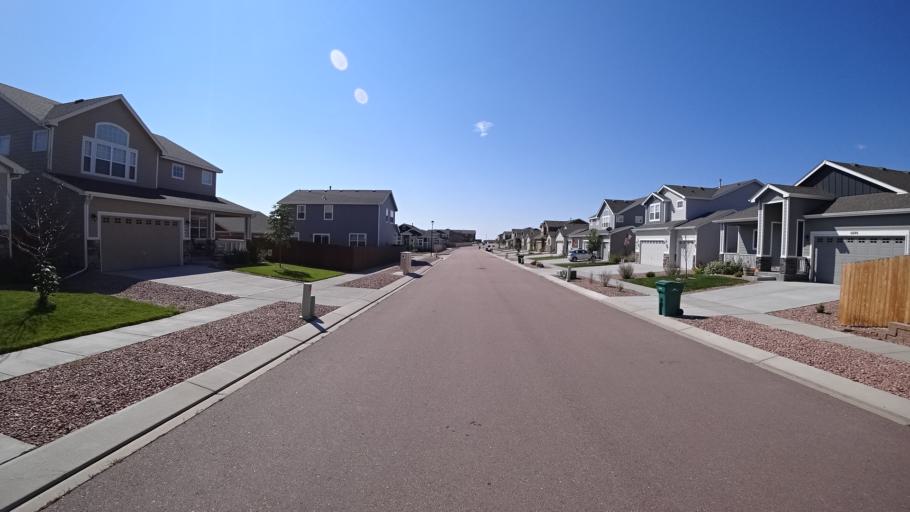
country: US
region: Colorado
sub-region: El Paso County
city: Cimarron Hills
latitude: 38.9318
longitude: -104.7098
